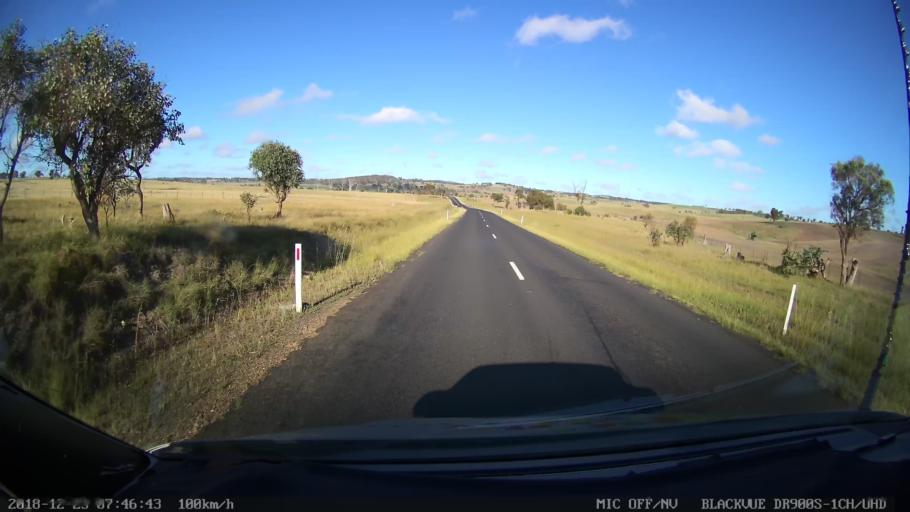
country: AU
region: New South Wales
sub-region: Armidale Dumaresq
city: Enmore
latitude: -30.5254
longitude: 151.9136
